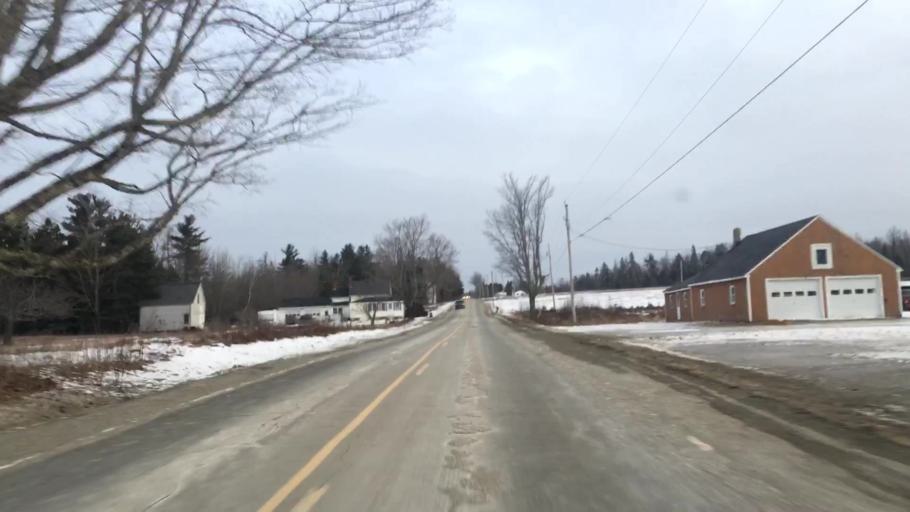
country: US
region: Maine
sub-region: Hancock County
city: Franklin
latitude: 44.7094
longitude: -68.3392
